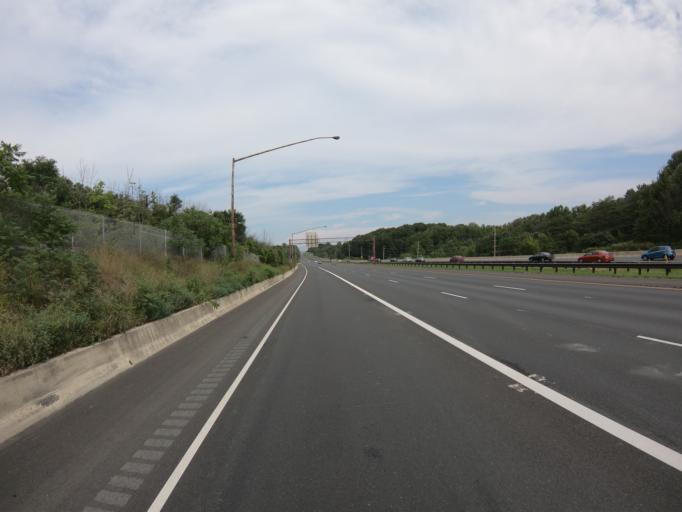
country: US
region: Maryland
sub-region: Montgomery County
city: Clarksburg
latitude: 39.2337
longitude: -77.2865
